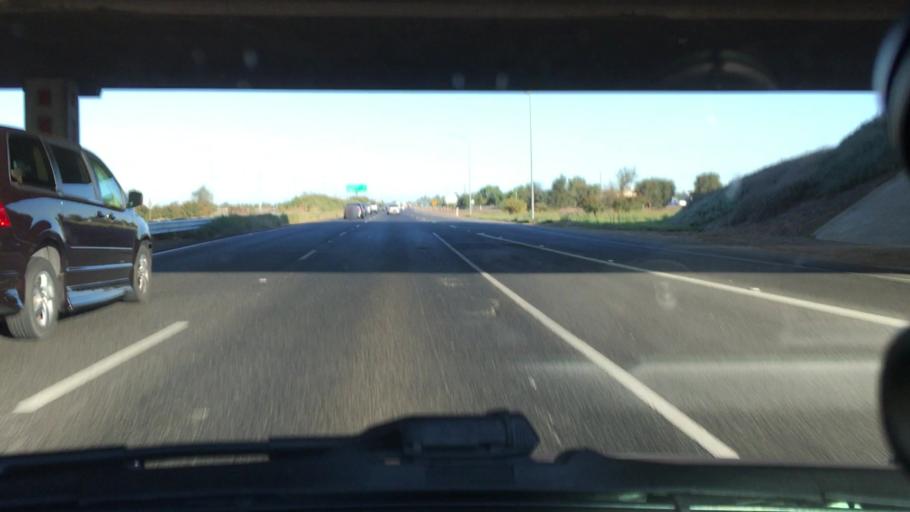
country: US
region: California
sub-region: Sacramento County
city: Elk Grove
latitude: 38.3764
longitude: -121.3619
